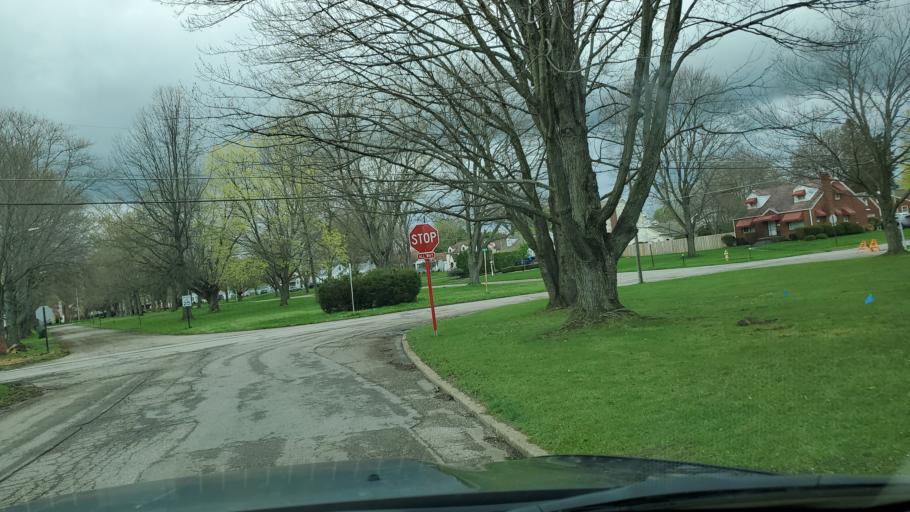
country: US
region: Ohio
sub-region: Mahoning County
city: Boardman
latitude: 41.0275
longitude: -80.6671
